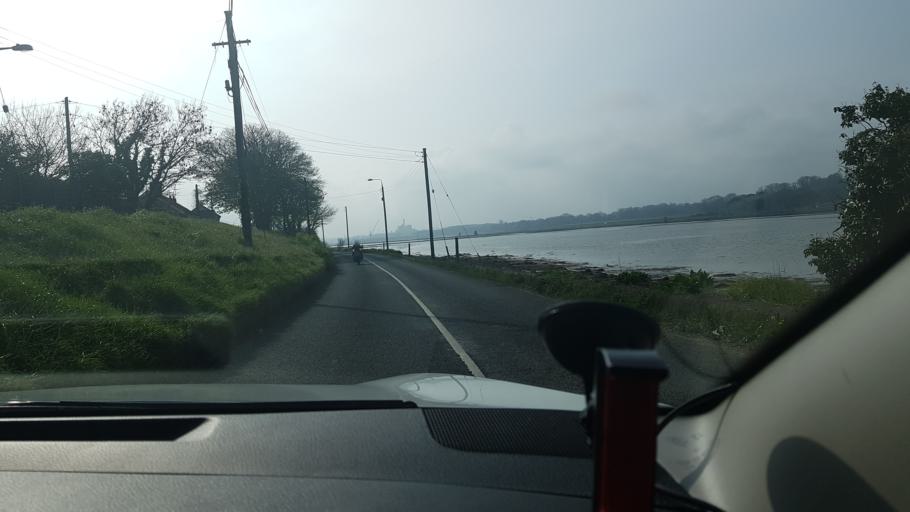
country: IE
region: Leinster
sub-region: Lu
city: Termonfeckin
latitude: 53.7233
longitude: -6.2755
